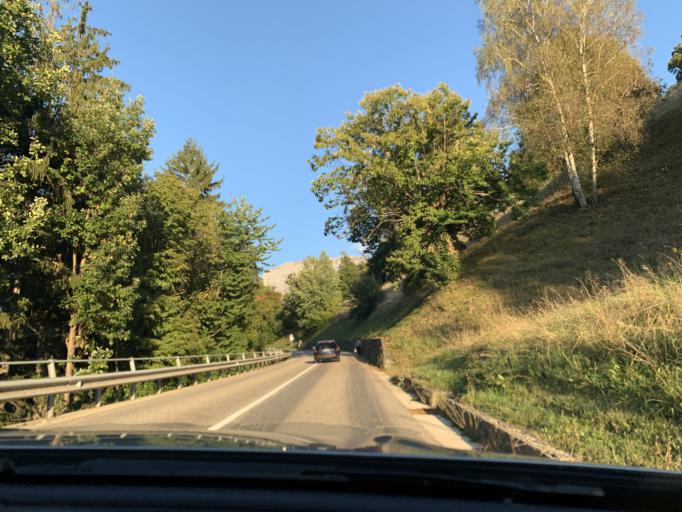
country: IT
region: Trentino-Alto Adige
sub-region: Bolzano
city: Fie Allo Sciliar
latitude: 46.5065
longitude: 11.4740
